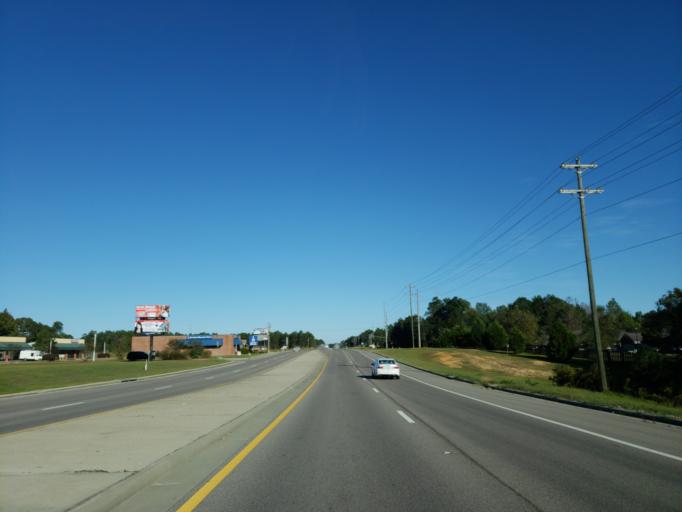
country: US
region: Mississippi
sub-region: Forrest County
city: Petal
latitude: 31.3503
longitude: -89.1992
